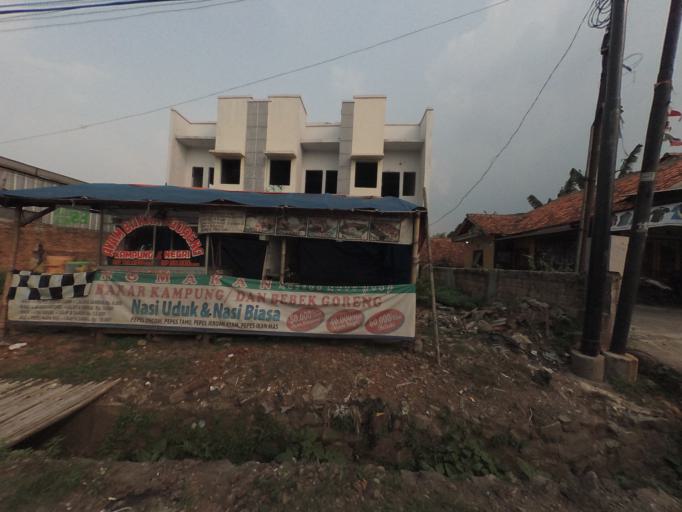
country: ID
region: West Java
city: Ciampea
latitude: -6.5700
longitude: 106.6683
